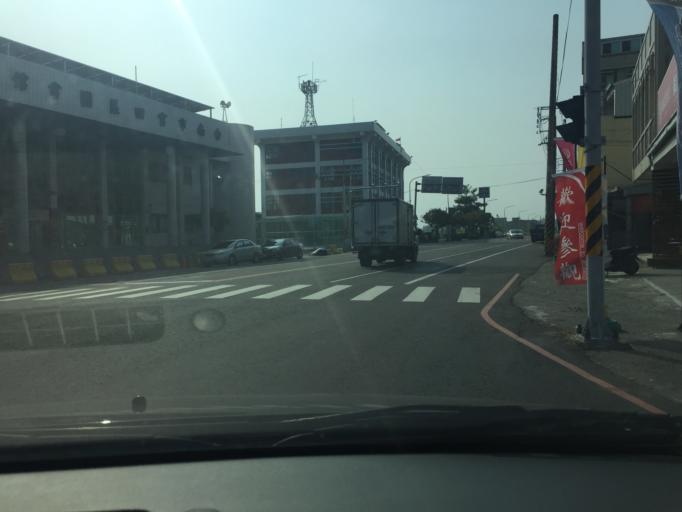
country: TW
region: Taiwan
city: Xinying
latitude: 23.1929
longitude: 120.3145
